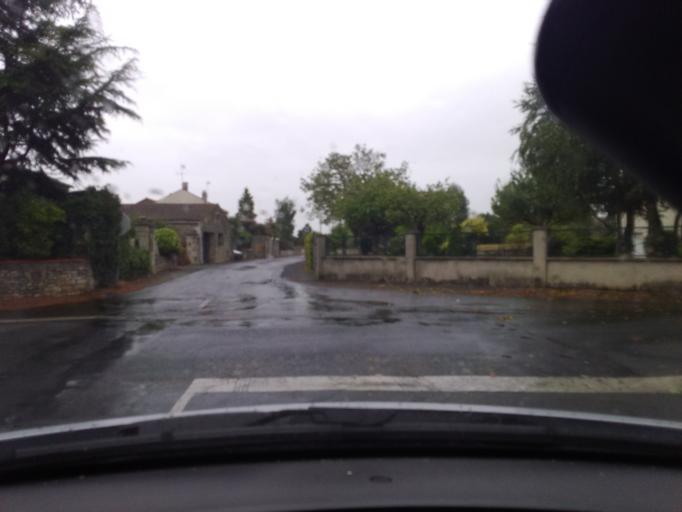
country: FR
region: Pays de la Loire
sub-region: Departement de la Vendee
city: Sainte-Gemme-la-Plaine
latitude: 46.4844
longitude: -1.1174
